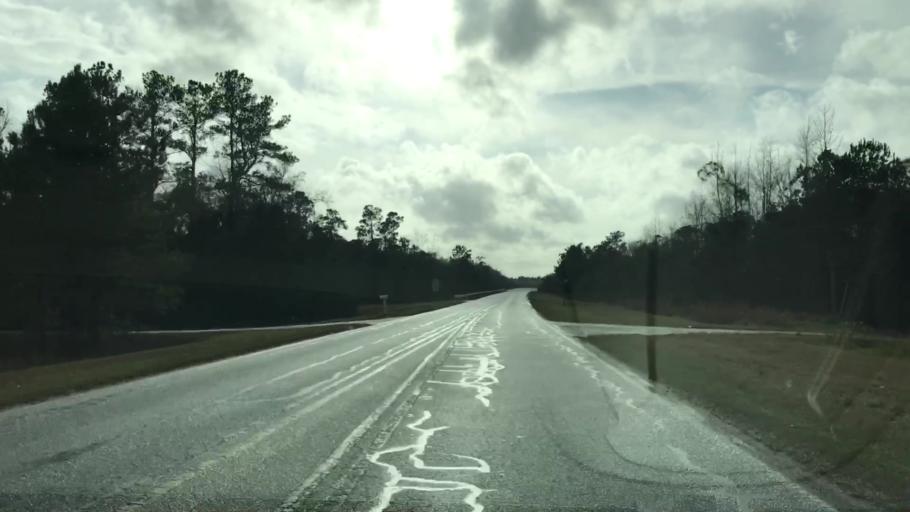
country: US
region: South Carolina
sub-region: Williamsburg County
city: Andrews
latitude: 33.4931
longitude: -79.5429
